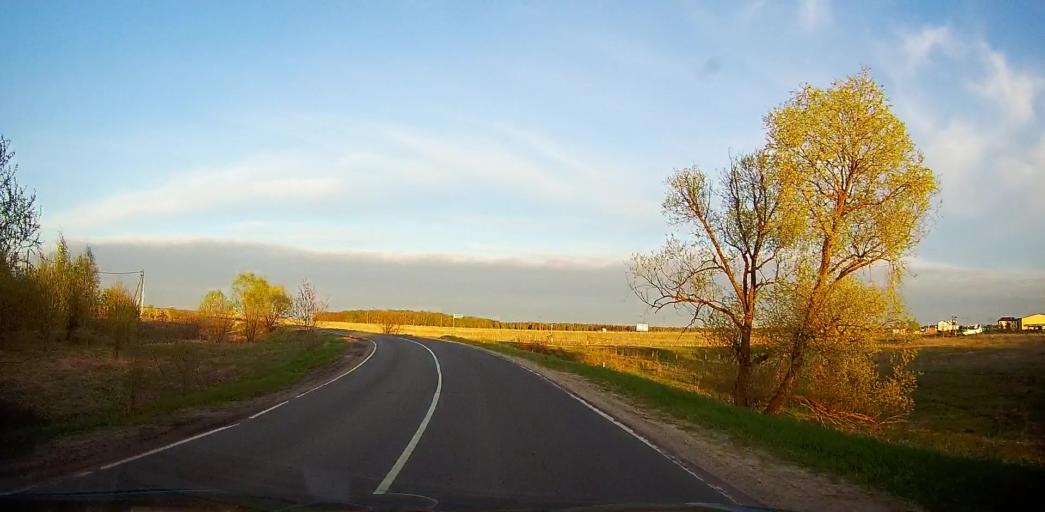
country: RU
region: Moskovskaya
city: Peski
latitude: 55.2104
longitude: 38.6751
